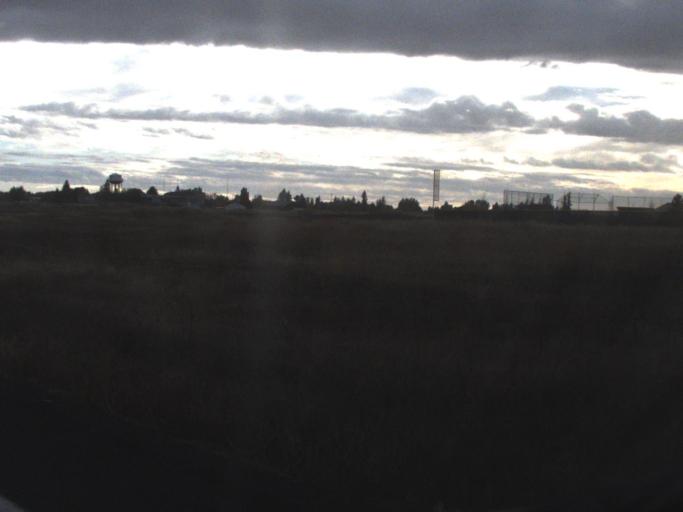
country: US
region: Washington
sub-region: Lincoln County
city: Davenport
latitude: 47.6636
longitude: -118.1410
